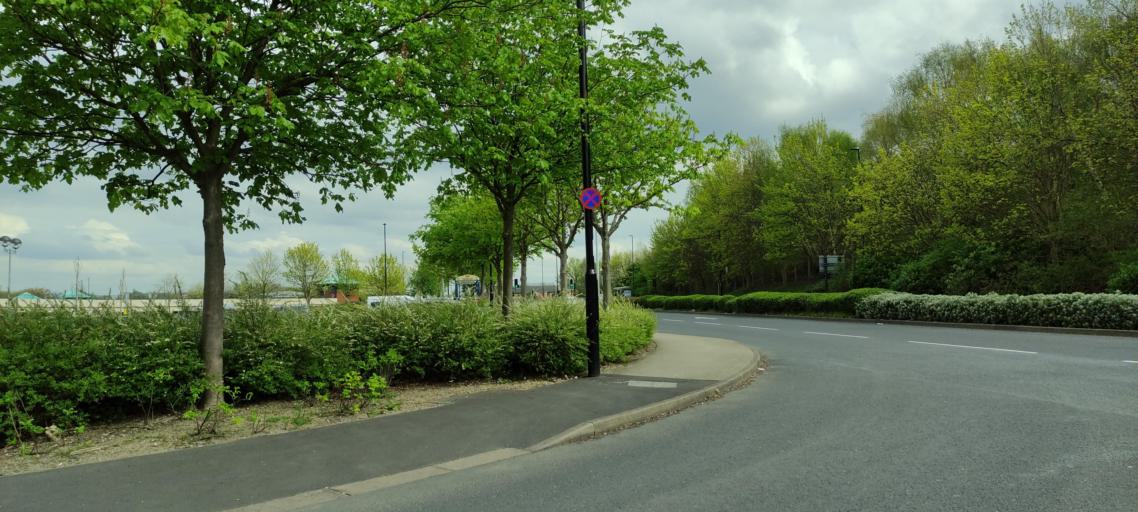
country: GB
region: England
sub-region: Rotherham
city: Orgreave
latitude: 53.4110
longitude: -1.4132
